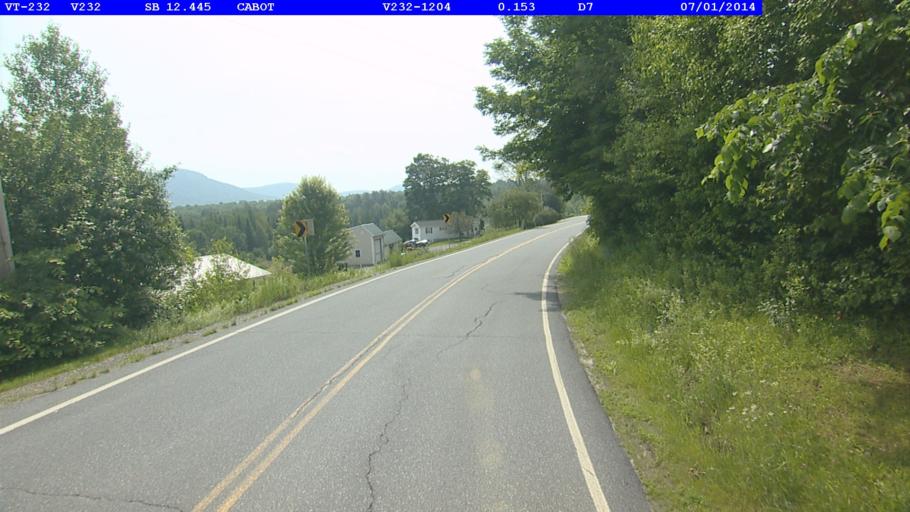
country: US
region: Vermont
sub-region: Caledonia County
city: Hardwick
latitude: 44.3563
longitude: -72.3081
